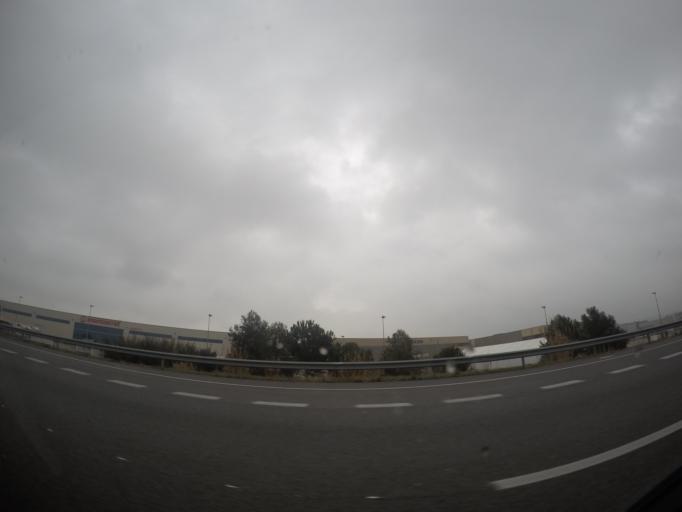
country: ES
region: Catalonia
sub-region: Provincia de Barcelona
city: Vilafranca del Penedes
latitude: 41.3286
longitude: 1.6763
